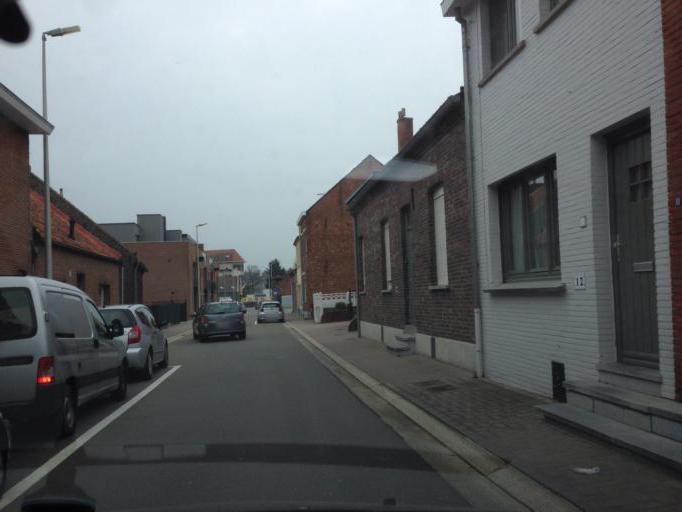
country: BE
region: Flanders
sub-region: Provincie Limburg
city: Bree
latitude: 51.1394
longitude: 5.5939
